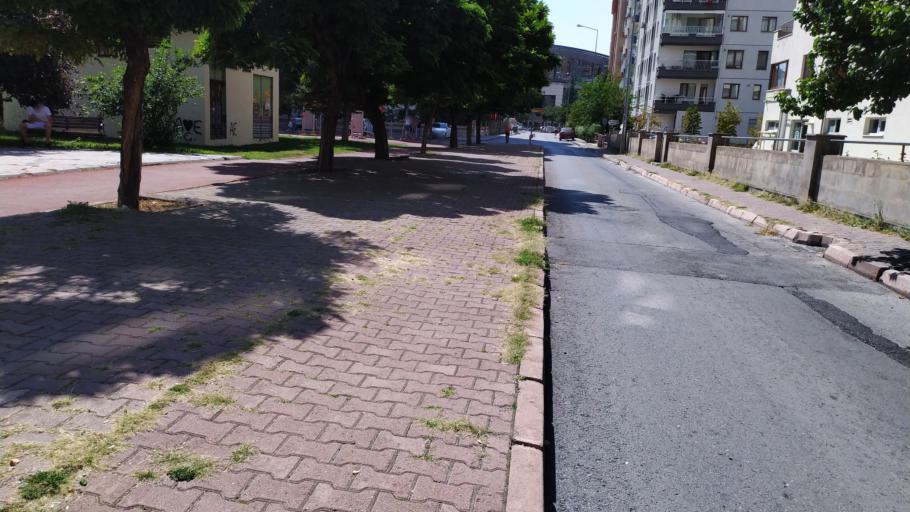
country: TR
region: Kayseri
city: Kayseri
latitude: 38.7281
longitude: 35.5213
